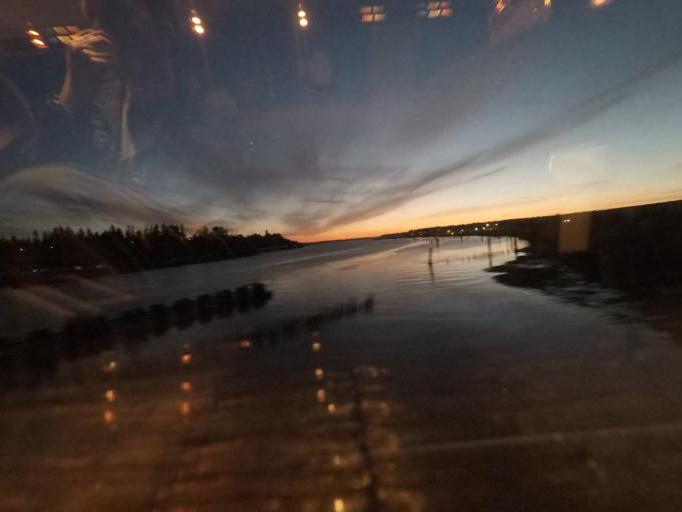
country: US
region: Washington
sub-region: Snohomish County
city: Marysville
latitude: 48.0179
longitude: -122.1887
